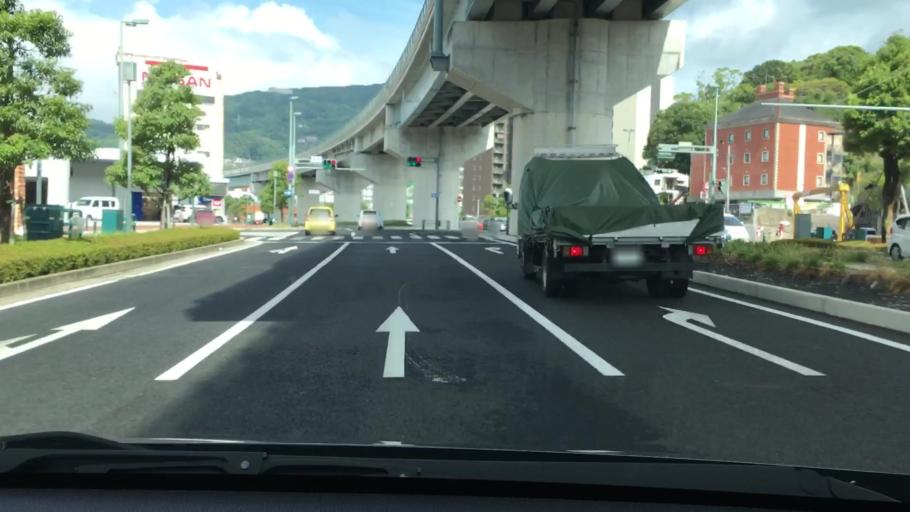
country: JP
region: Nagasaki
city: Sasebo
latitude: 33.1673
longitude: 129.7210
